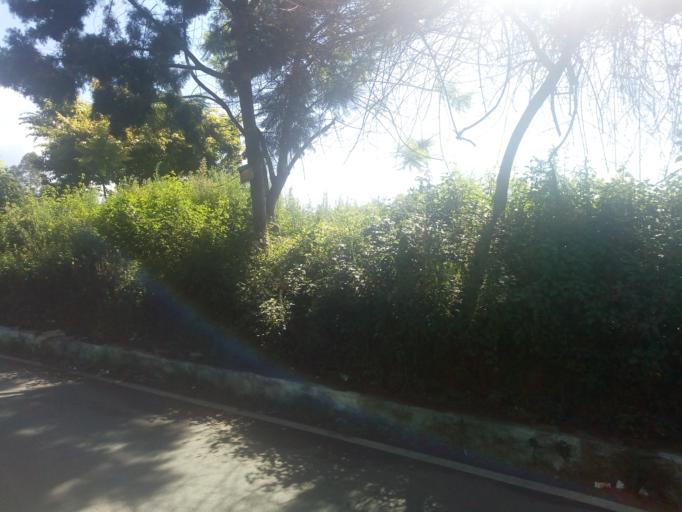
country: IN
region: Tamil Nadu
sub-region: Nilgiri
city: Wellington
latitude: 11.3446
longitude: 76.7902
